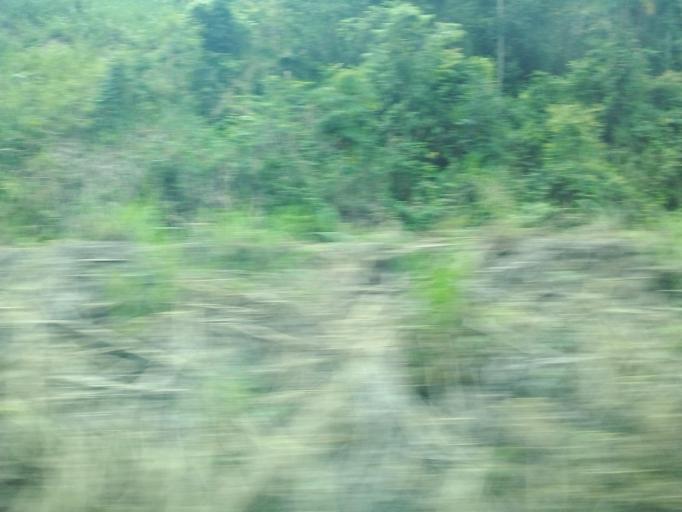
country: BR
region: Minas Gerais
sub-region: Rio Piracicaba
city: Rio Piracicaba
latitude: -19.8971
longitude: -43.1432
